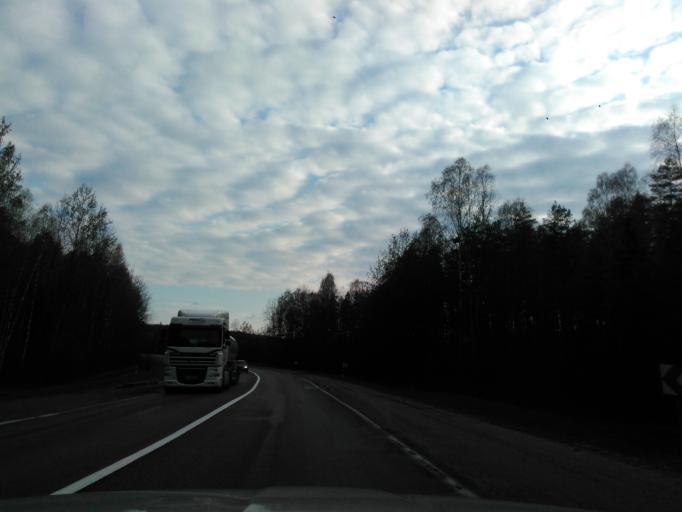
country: BY
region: Minsk
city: Plyeshchanitsy
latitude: 54.3514
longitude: 27.8807
